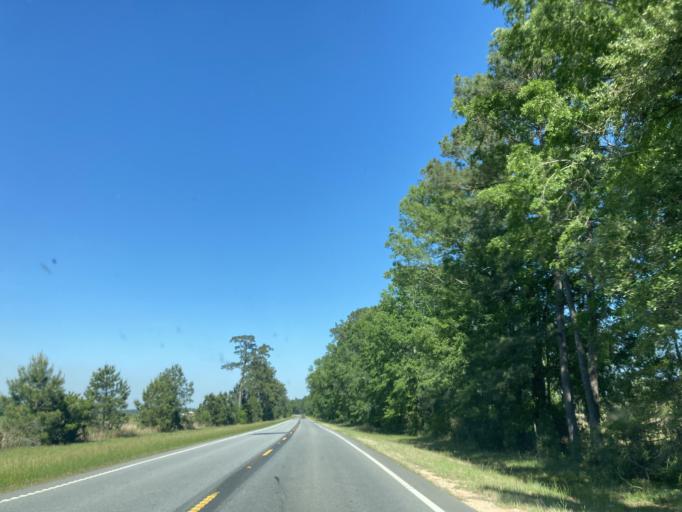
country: US
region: Georgia
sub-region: Baker County
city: Newton
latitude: 31.3319
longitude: -84.3266
